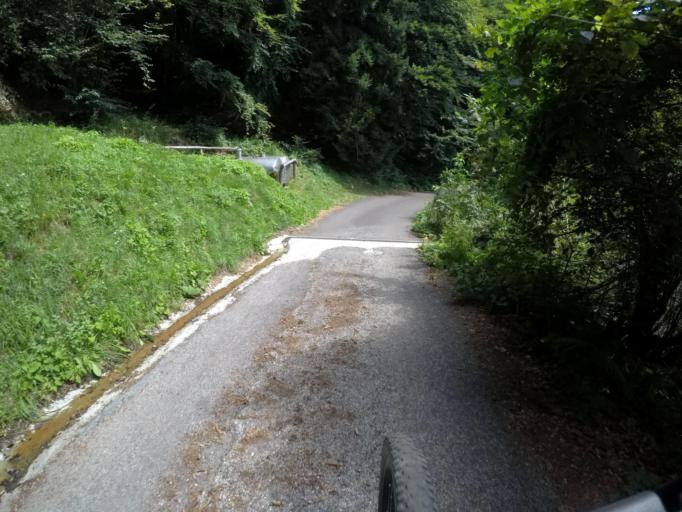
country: IT
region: Friuli Venezia Giulia
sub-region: Provincia di Udine
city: Ligosullo
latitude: 46.4909
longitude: 13.0741
